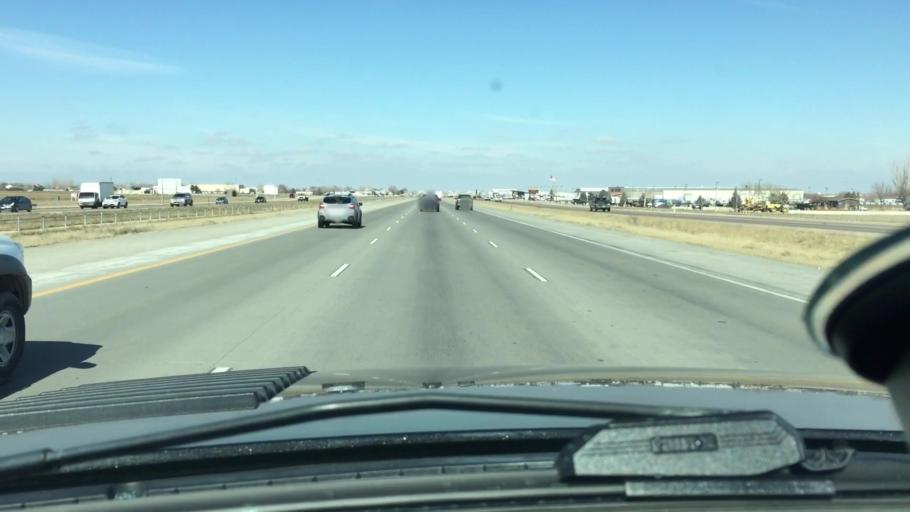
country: US
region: Colorado
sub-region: Weld County
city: Frederick
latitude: 40.1058
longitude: -104.9799
